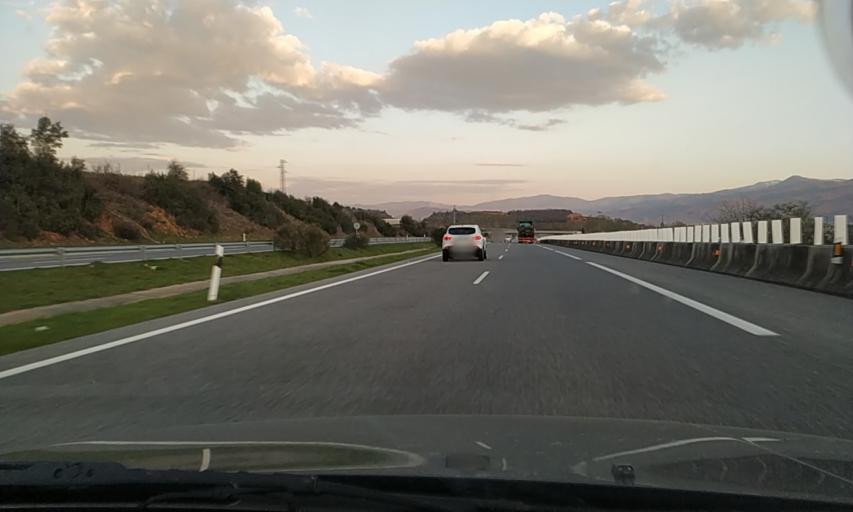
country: ES
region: Castille and Leon
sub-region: Provincia de Leon
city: Villadecanes
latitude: 42.5770
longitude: -6.7783
